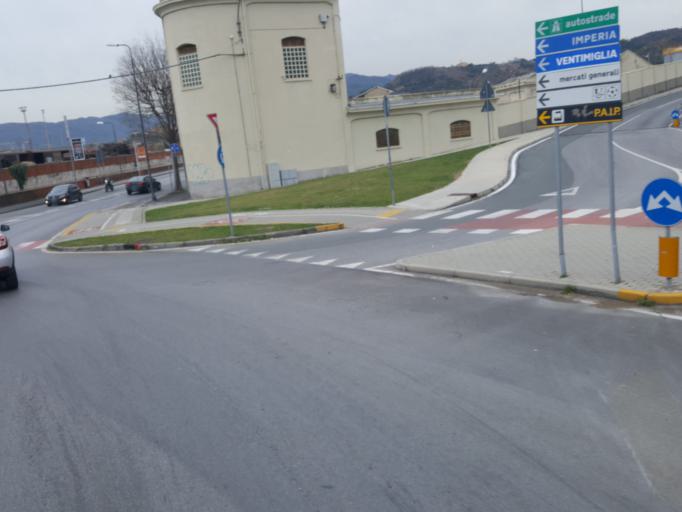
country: IT
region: Liguria
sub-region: Provincia di Savona
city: Savona
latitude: 44.2990
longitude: 8.4625
